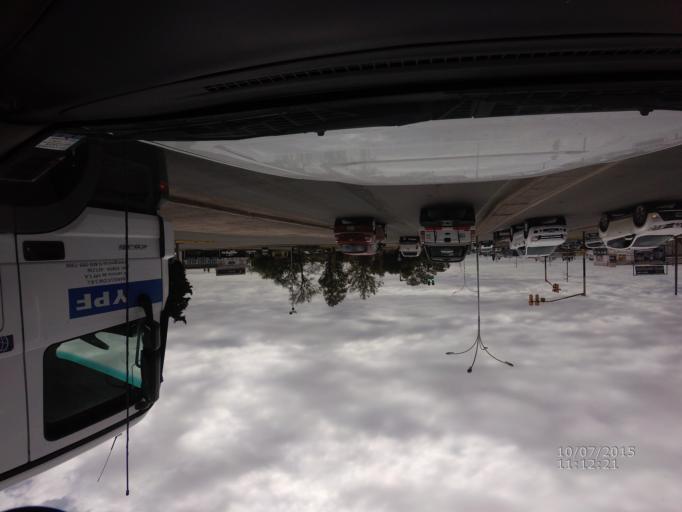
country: AR
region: Cordoba
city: Jesus Maria
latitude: -30.9843
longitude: -64.0883
